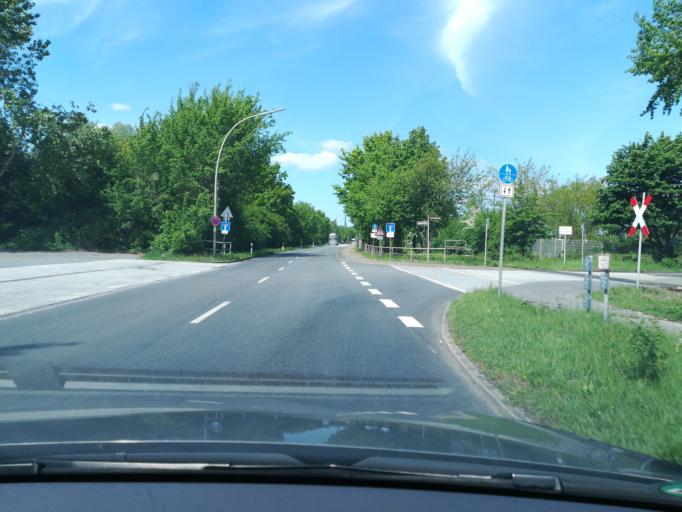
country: DE
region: Hamburg
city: Altona
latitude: 53.5041
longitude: 9.9447
